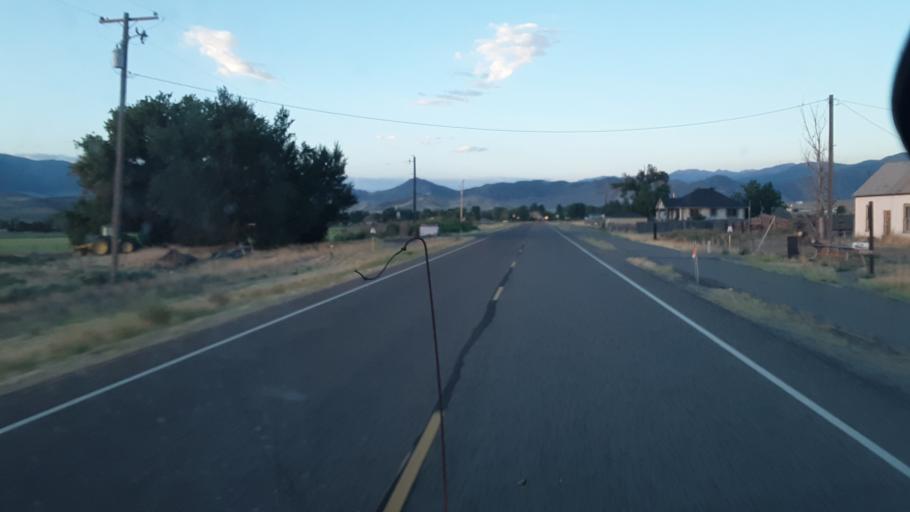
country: US
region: Utah
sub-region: Sevier County
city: Monroe
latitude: 38.6359
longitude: -112.2171
